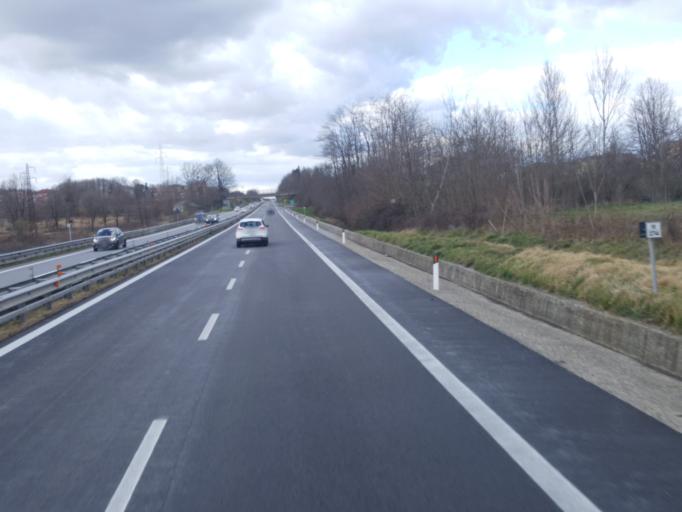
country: IT
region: Calabria
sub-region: Provincia di Cosenza
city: Santo Stefano di Rogliano
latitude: 39.2054
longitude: 16.3100
